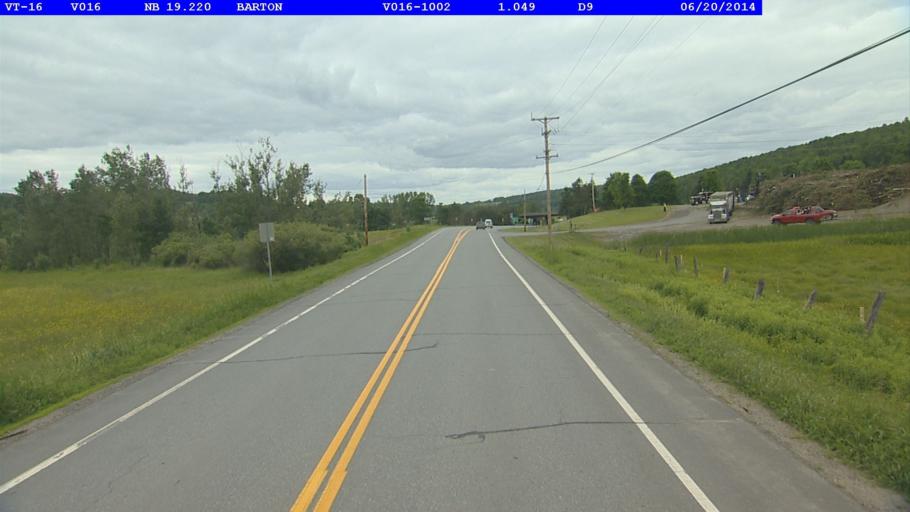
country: US
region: Vermont
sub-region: Orleans County
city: Newport
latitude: 44.7325
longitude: -72.1844
